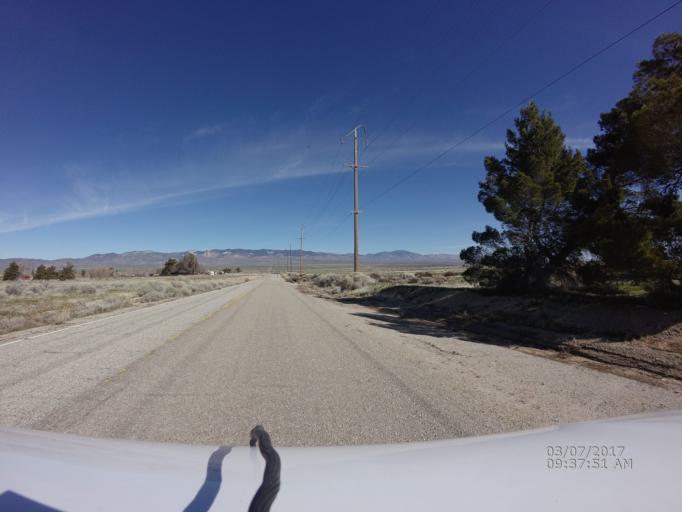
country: US
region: California
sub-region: Los Angeles County
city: Green Valley
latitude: 34.7809
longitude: -118.6070
